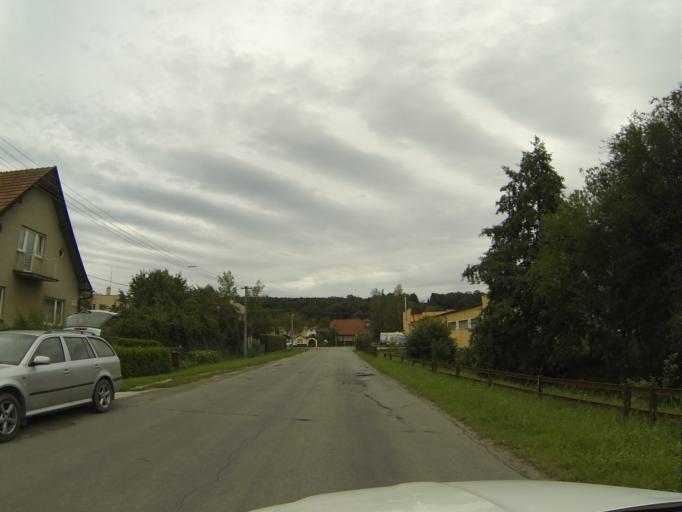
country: SK
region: Nitriansky
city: Prievidza
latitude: 48.7864
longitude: 18.6335
